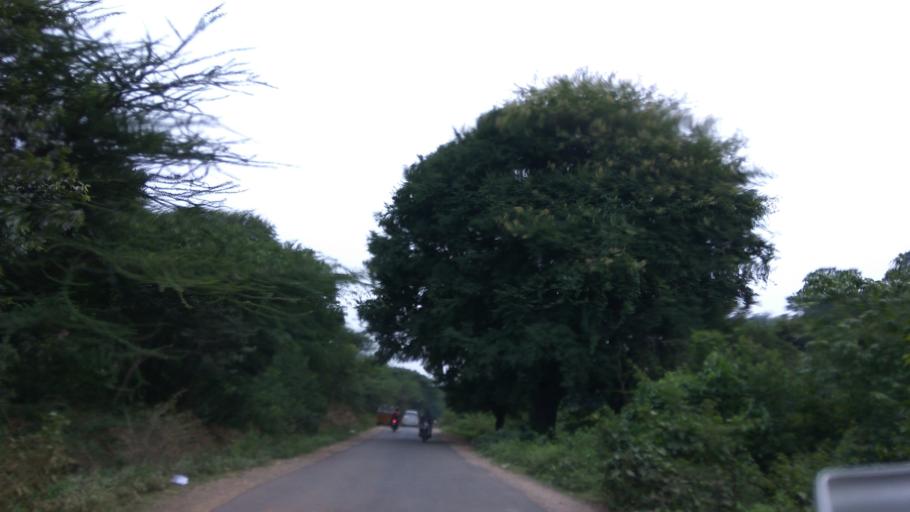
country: IN
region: Tamil Nadu
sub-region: Dharmapuri
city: Mallapuram
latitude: 12.0098
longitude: 78.1336
